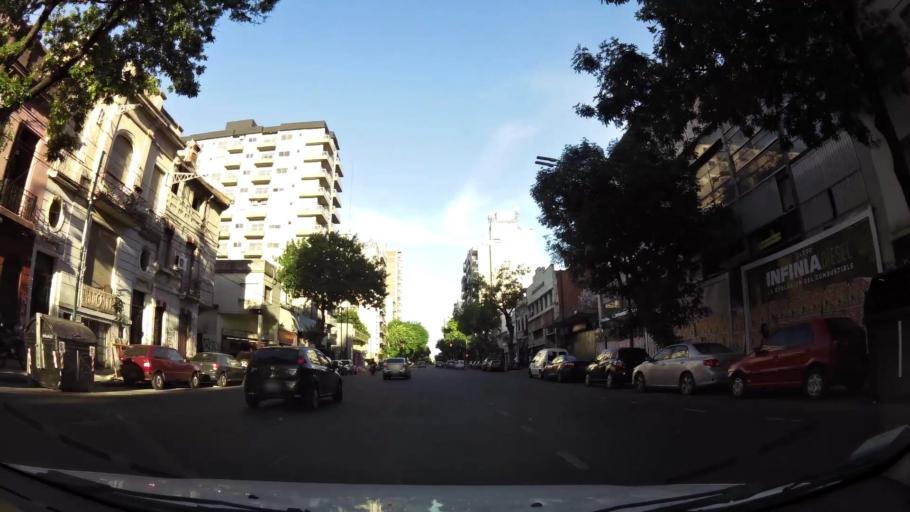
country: AR
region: Buenos Aires F.D.
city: Colegiales
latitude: -34.6088
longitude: -58.4273
